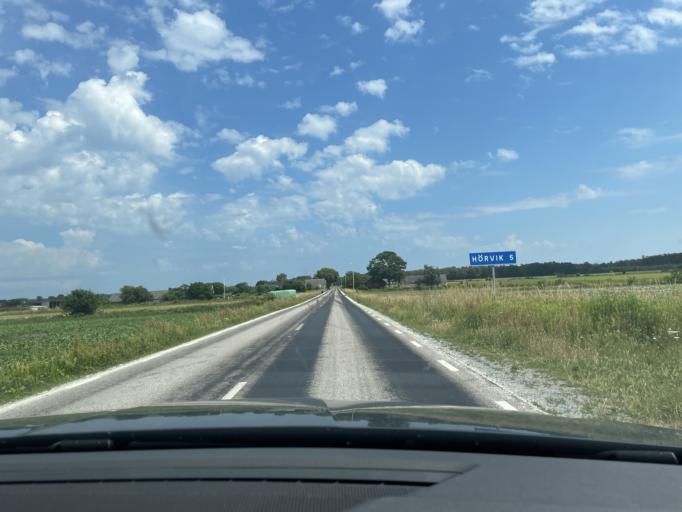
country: SE
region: Blekinge
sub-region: Solvesborgs Kommun
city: Soelvesborg
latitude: 56.0403
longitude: 14.6944
